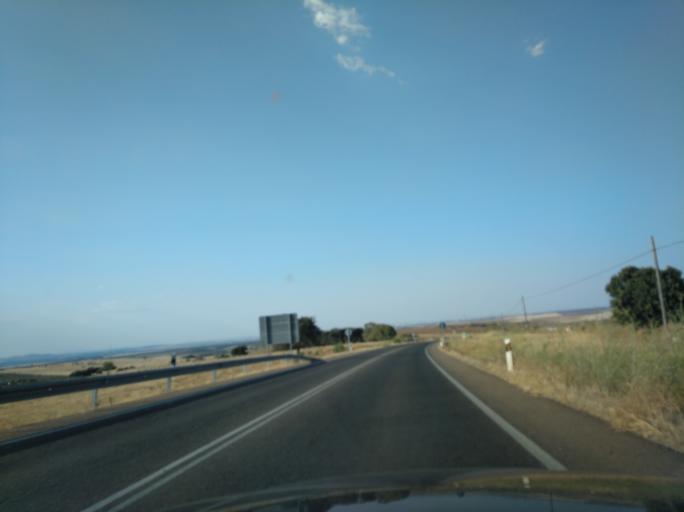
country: ES
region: Extremadura
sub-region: Provincia de Badajoz
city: Olivenza
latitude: 38.7181
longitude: -7.0840
